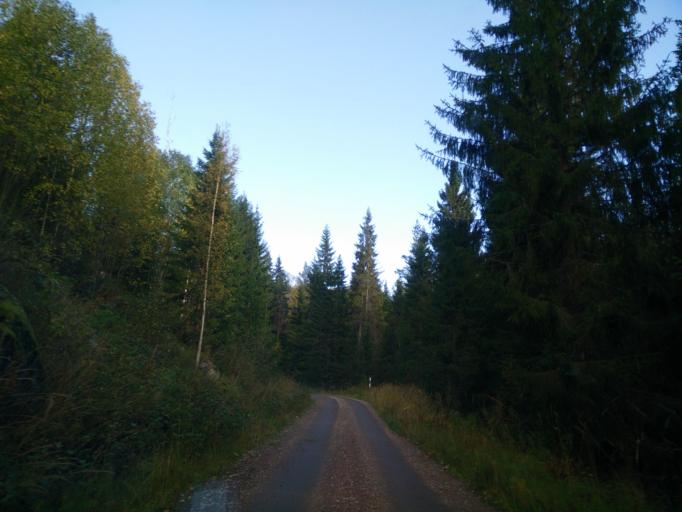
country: SE
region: Vaesternorrland
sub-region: Sundsvalls Kommun
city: Matfors
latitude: 62.3285
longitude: 16.9067
